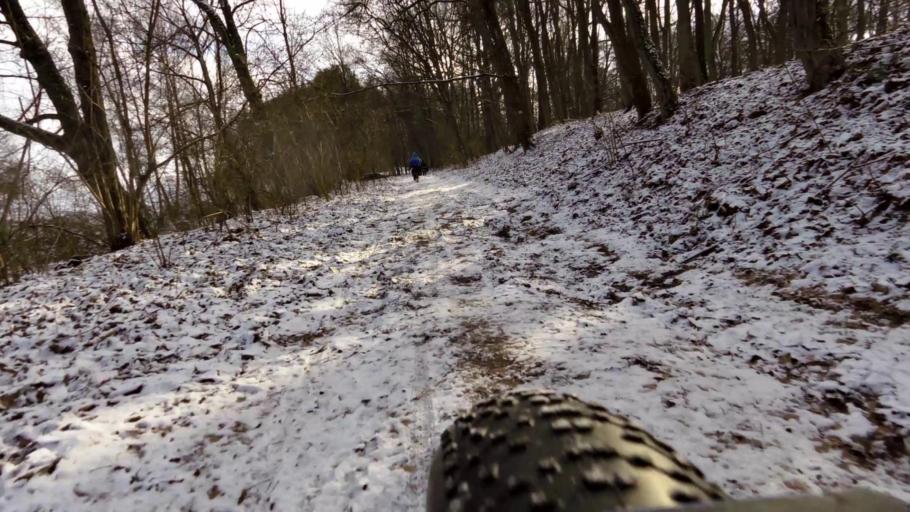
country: PL
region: West Pomeranian Voivodeship
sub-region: Powiat walecki
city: Tuczno
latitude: 53.3026
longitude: 16.2733
